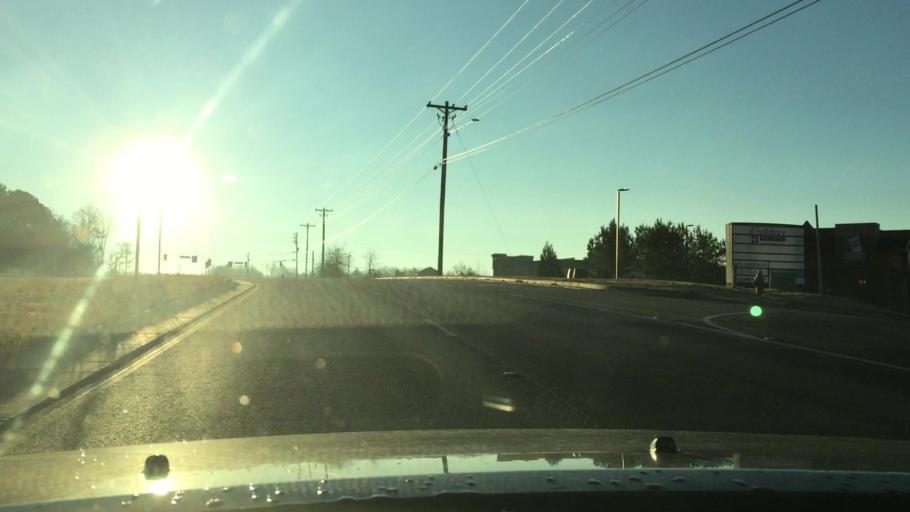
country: US
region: Georgia
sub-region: Forsyth County
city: Cumming
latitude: 34.1739
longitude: -84.1886
